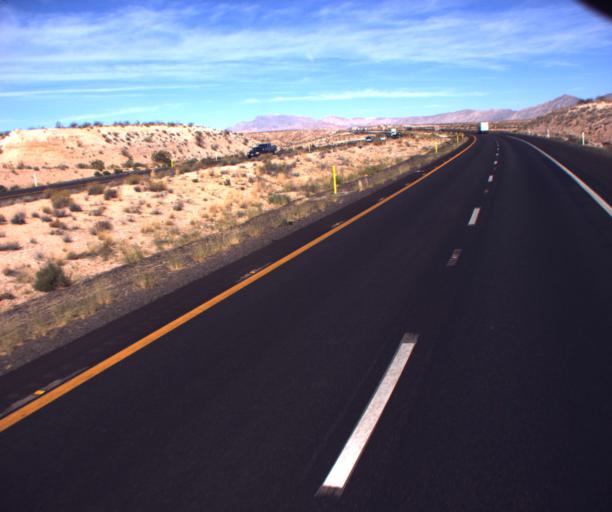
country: US
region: Nevada
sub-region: Clark County
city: Mesquite
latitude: 36.8306
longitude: -114.0077
